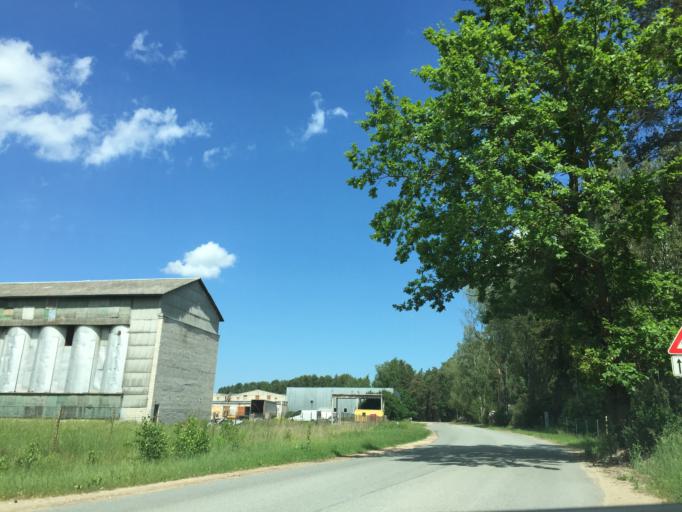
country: LV
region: Babite
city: Pinki
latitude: 56.8714
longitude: 23.9527
